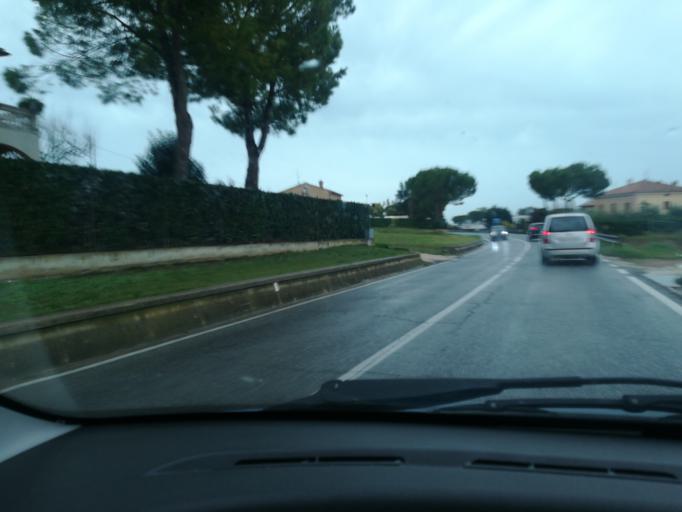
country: IT
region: The Marches
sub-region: Provincia di Macerata
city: Santa Maria Apparente
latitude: 43.2941
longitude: 13.6755
